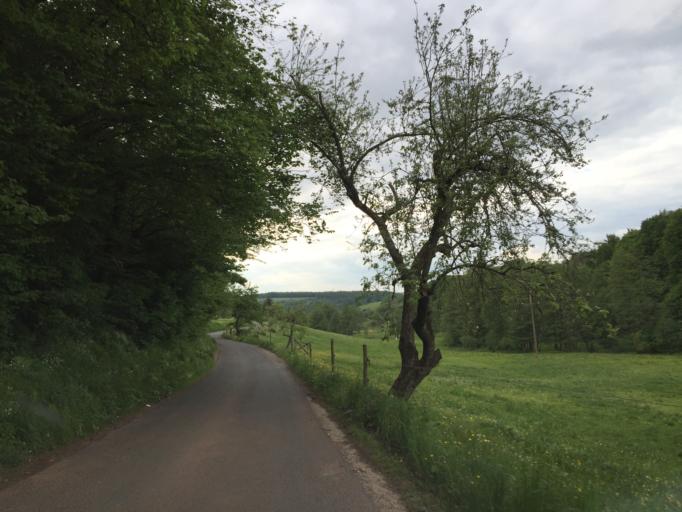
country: DE
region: Bavaria
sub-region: Regierungsbezirk Unterfranken
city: Waldaschaff
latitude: 49.9596
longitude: 9.2719
